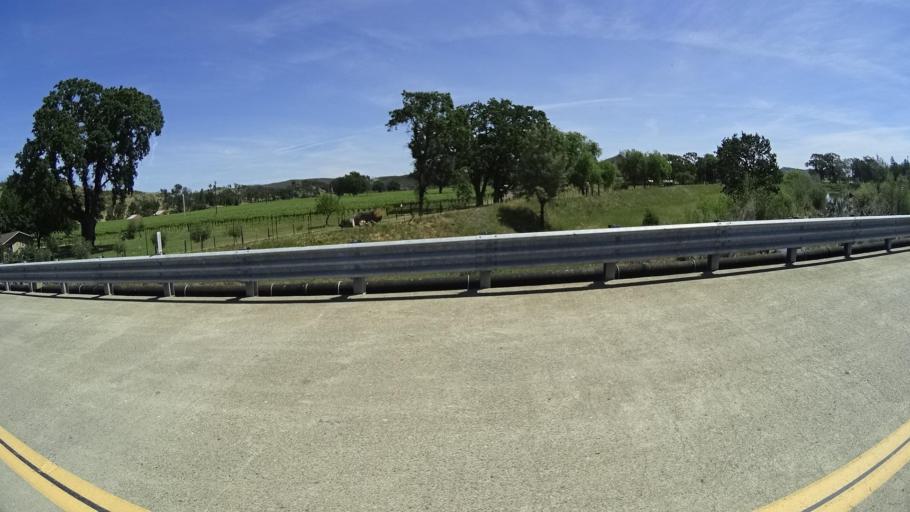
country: US
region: California
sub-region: Lake County
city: Middletown
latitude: 38.7602
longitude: -122.6154
